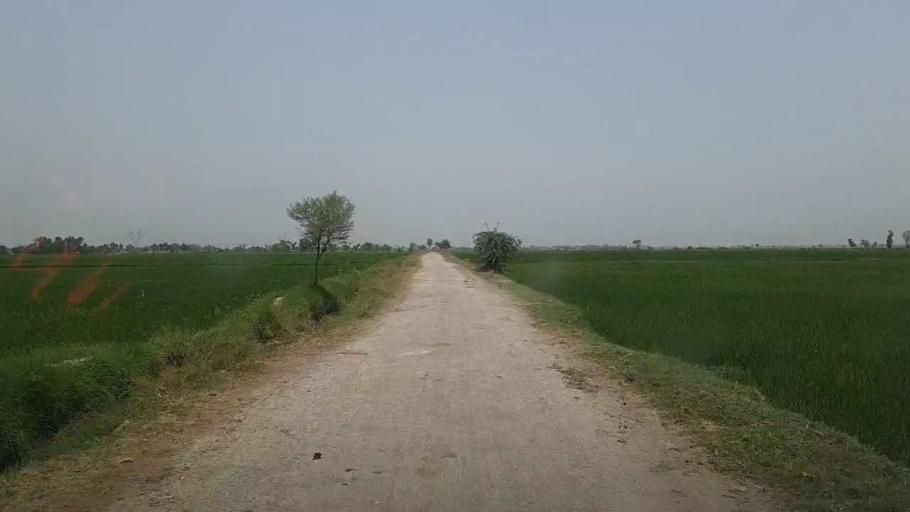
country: PK
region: Sindh
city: Sita Road
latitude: 27.0584
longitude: 67.8487
